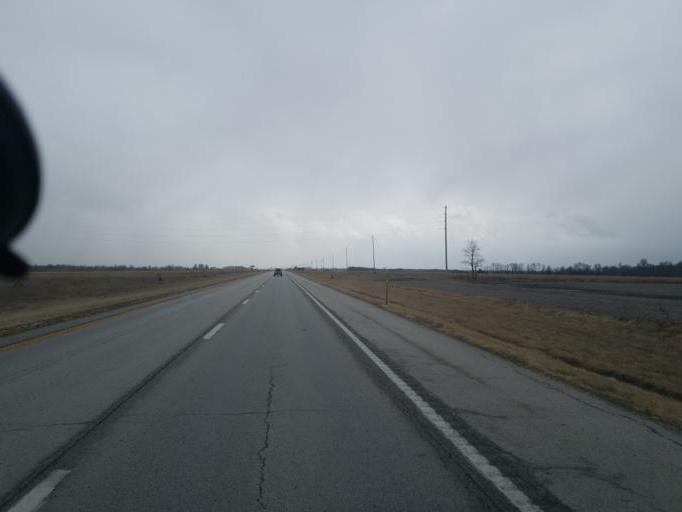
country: US
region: Missouri
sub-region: Randolph County
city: Moberly
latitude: 39.5570
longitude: -92.4578
